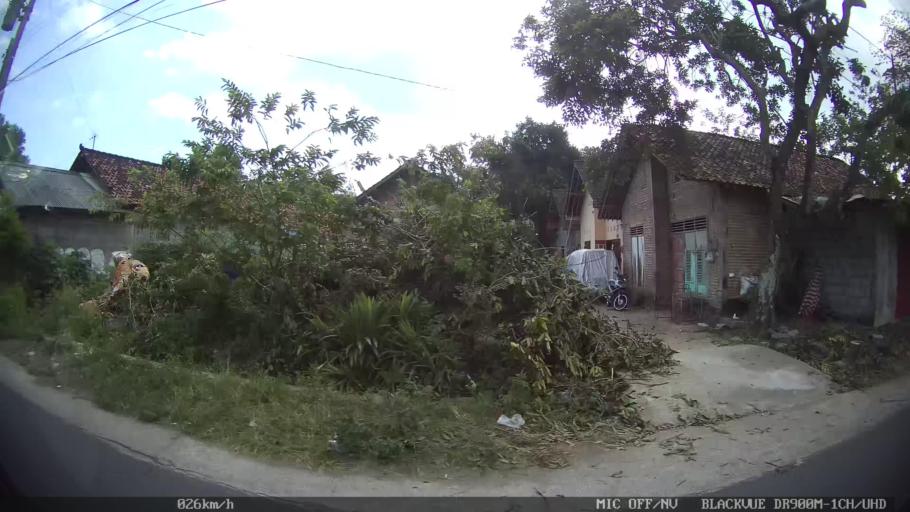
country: ID
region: Daerah Istimewa Yogyakarta
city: Gamping Lor
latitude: -7.7931
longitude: 110.3365
